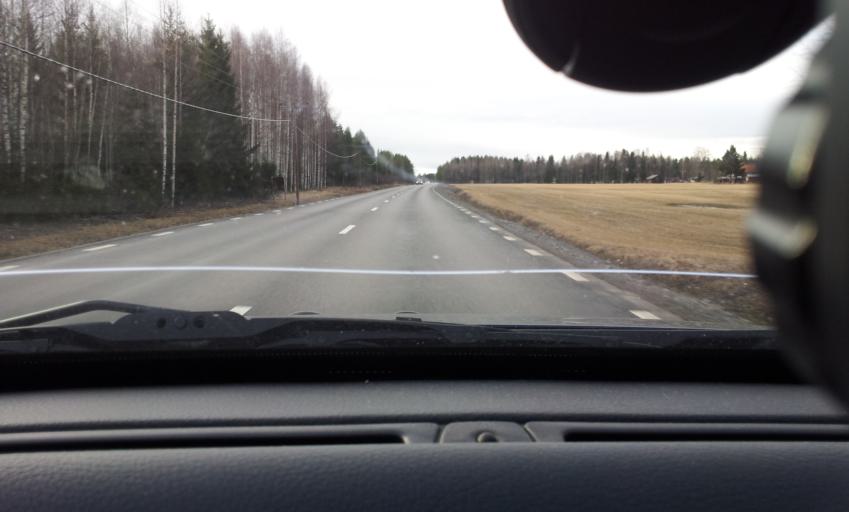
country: SE
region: Gaevleborg
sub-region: Ljusdals Kommun
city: Farila
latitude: 61.8679
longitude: 15.7308
